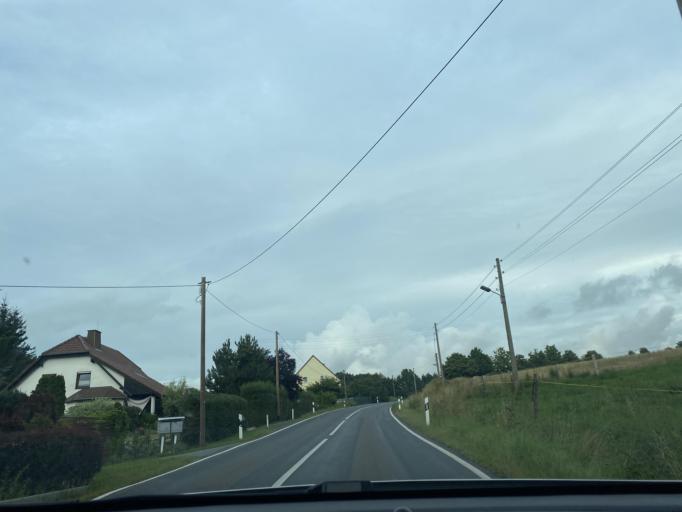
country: DE
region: Saxony
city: Grosshennersdorf
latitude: 51.0203
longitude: 14.7897
